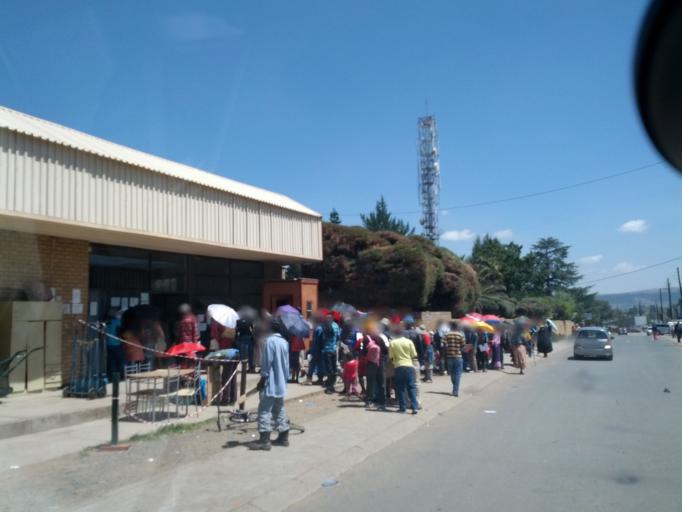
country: LS
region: Butha-Buthe
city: Butha-Buthe
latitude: -28.7639
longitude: 28.2490
